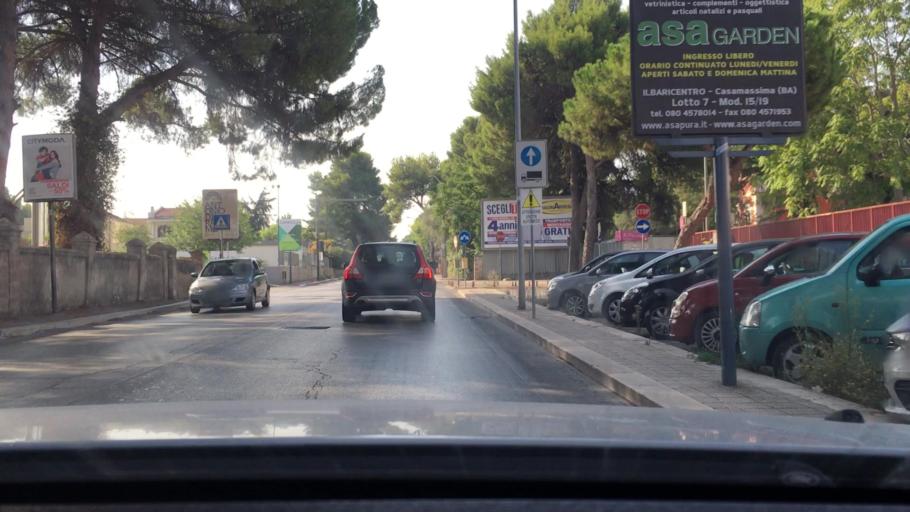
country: IT
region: Apulia
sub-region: Provincia di Bari
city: Bari
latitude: 41.0985
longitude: 16.8895
